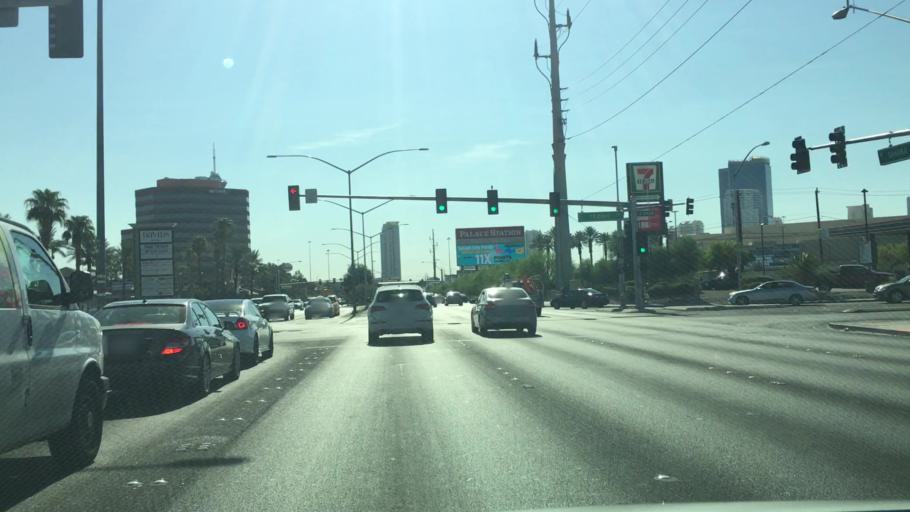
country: US
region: Nevada
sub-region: Clark County
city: Las Vegas
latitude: 36.1443
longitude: -115.1779
